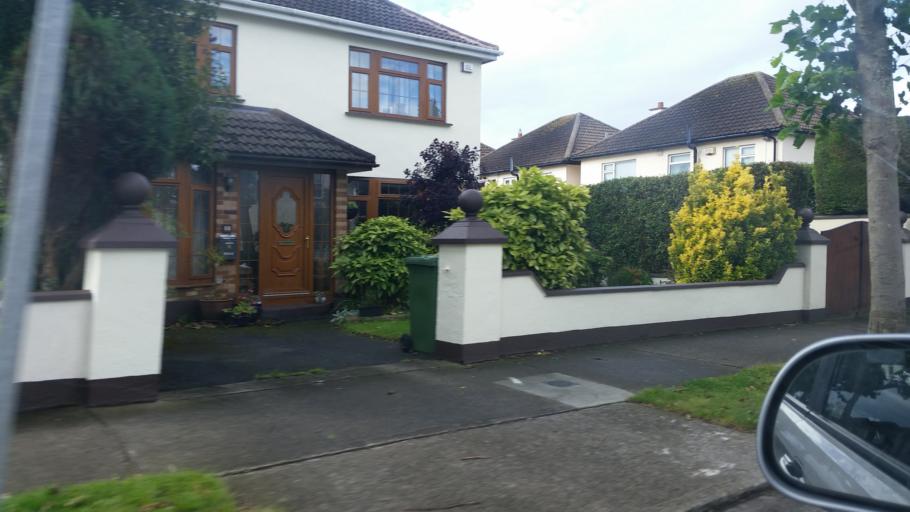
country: IE
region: Leinster
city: Portmarnock
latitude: 53.4349
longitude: -6.1360
